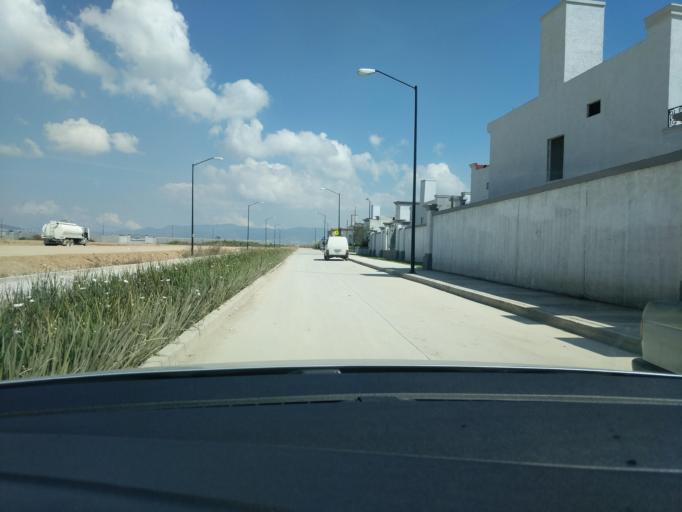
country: MX
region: Hidalgo
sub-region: Zempoala
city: Jagueey de Tellez (Estacion Tellez)
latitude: 20.0047
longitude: -98.7742
